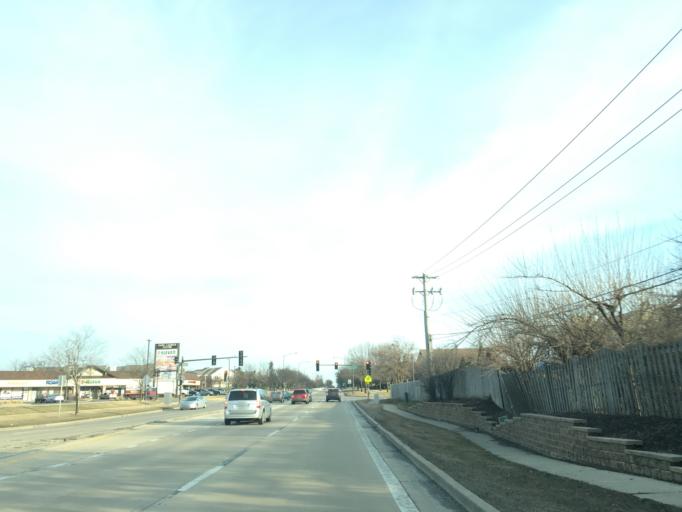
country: US
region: Illinois
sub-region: Cook County
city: Streamwood
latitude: 42.0313
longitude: -88.1564
